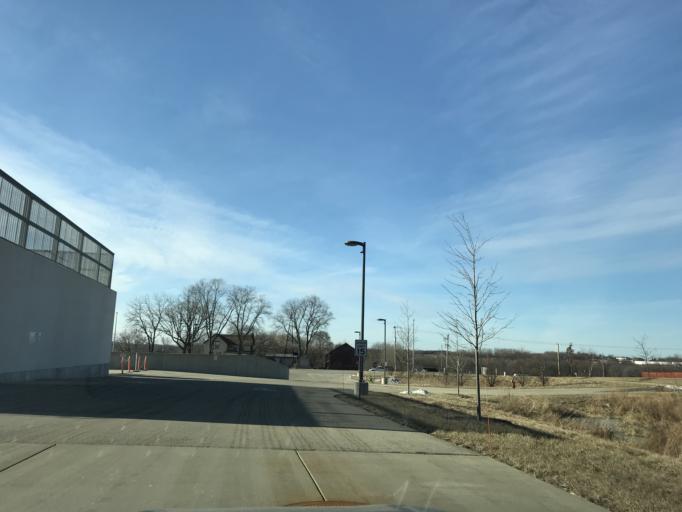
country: US
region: Wisconsin
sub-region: Dane County
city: Windsor
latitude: 43.1555
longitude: -89.3037
